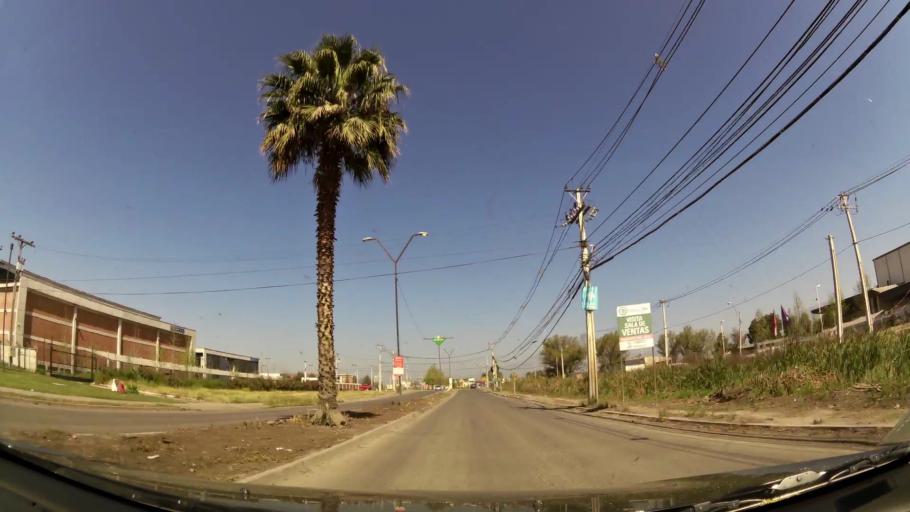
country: CL
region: Santiago Metropolitan
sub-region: Provincia de Chacabuco
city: Chicureo Abajo
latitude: -33.3230
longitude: -70.7399
